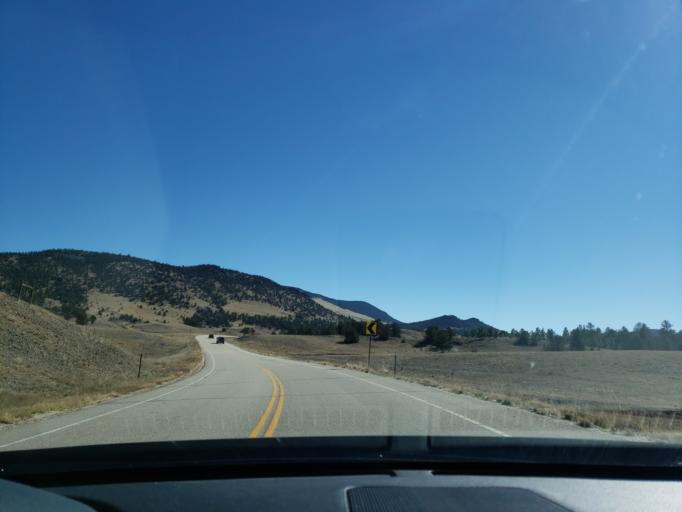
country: US
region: Colorado
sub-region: Chaffee County
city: Buena Vista
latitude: 38.8632
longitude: -105.6629
